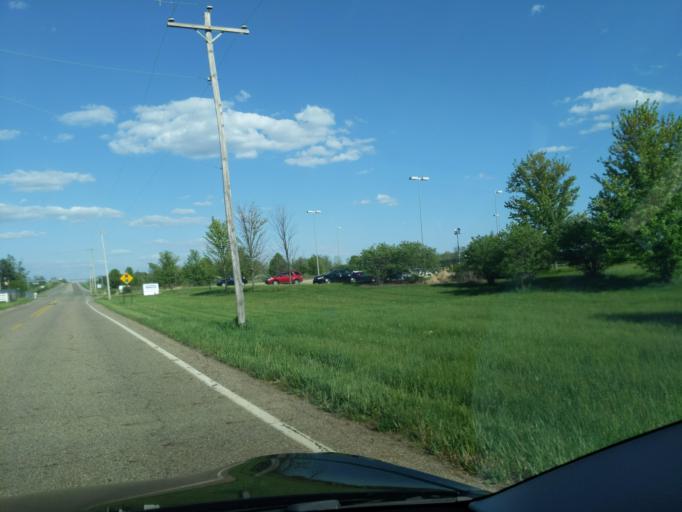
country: US
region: Michigan
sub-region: Eaton County
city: Dimondale
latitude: 42.6829
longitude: -84.6848
